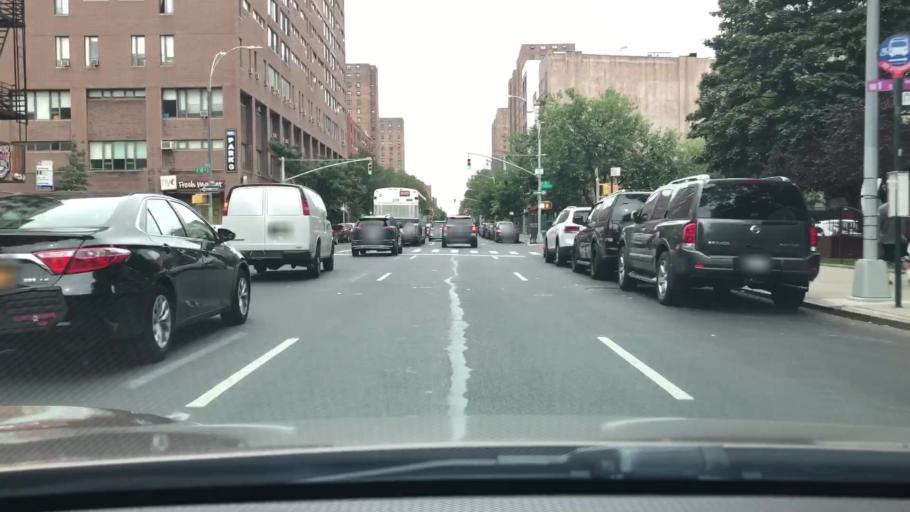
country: US
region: New York
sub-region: New York County
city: Manhattan
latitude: 40.7958
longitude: -73.9479
